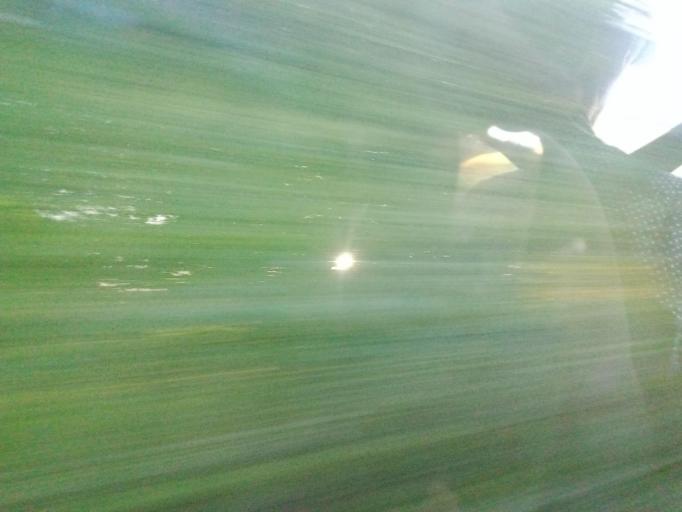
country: IE
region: Leinster
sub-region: Kilkenny
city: Kilkenny
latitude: 52.7274
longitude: -7.2366
